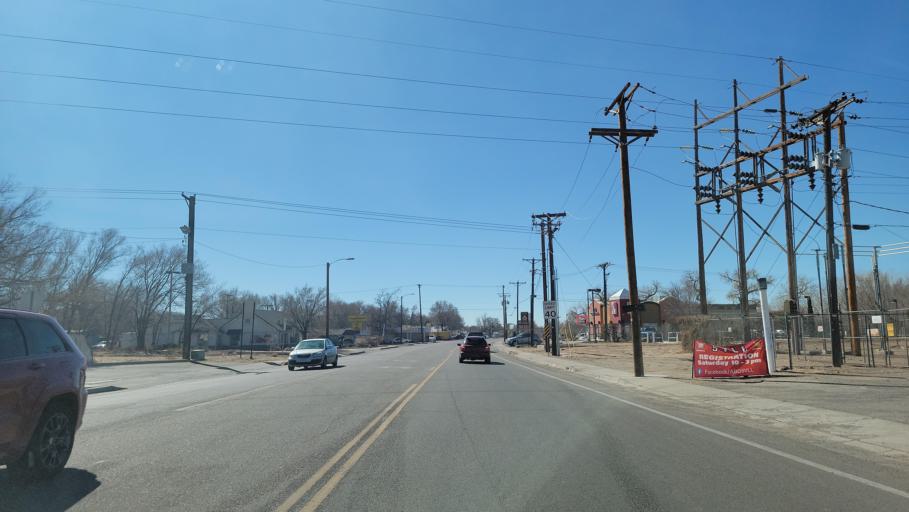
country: US
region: New Mexico
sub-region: Bernalillo County
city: South Valley
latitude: 35.0255
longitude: -106.6808
